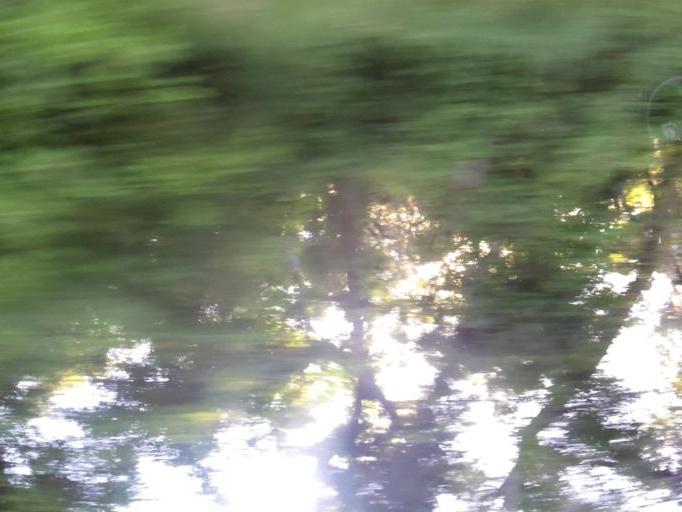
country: US
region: Florida
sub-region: Duval County
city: Atlantic Beach
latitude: 30.3702
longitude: -81.5147
